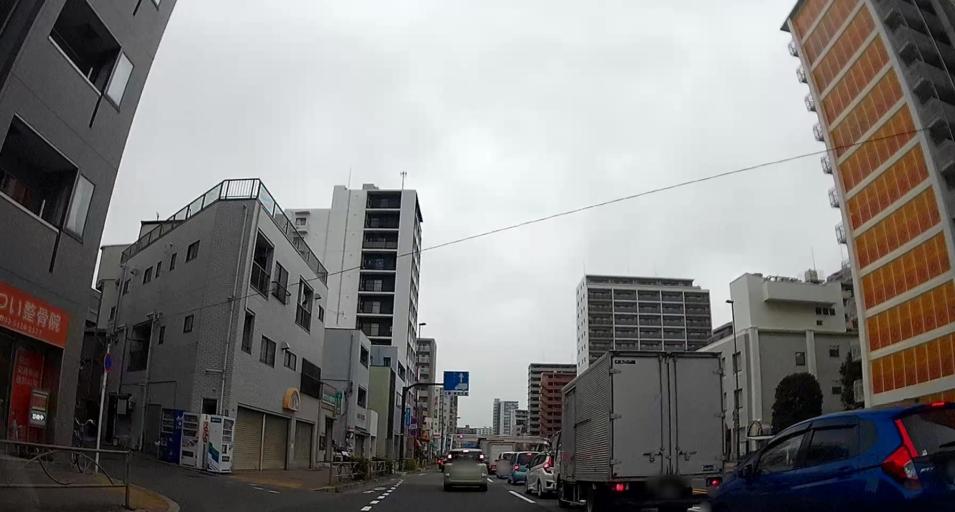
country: JP
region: Tokyo
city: Urayasu
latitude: 35.6974
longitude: 139.8386
